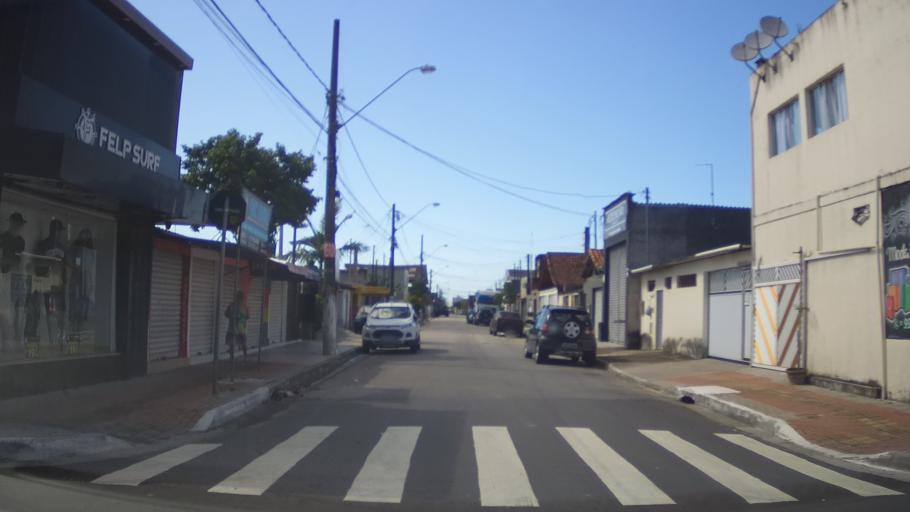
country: BR
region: Sao Paulo
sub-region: Mongagua
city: Mongagua
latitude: -24.0304
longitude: -46.5239
